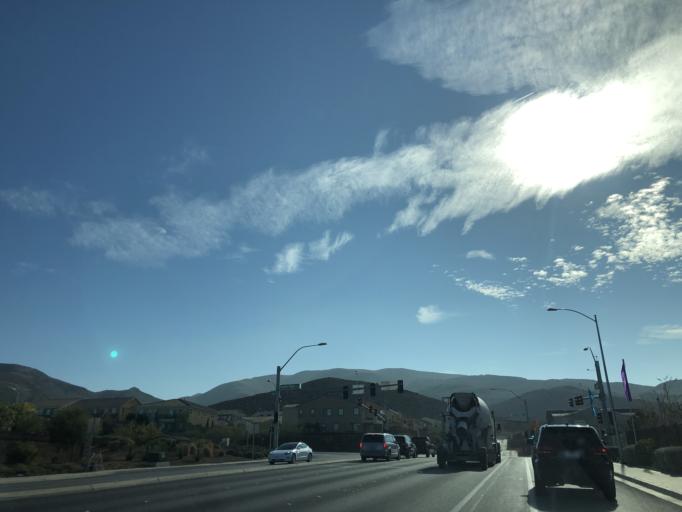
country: US
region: Nevada
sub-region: Clark County
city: Henderson
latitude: 36.0228
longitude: -115.0297
